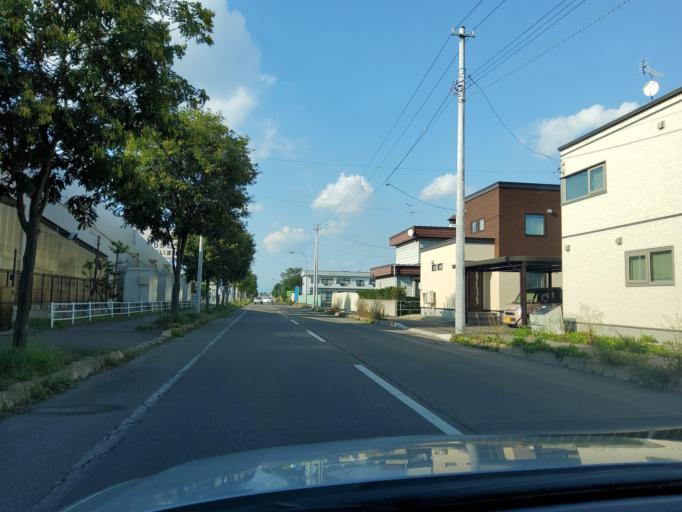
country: JP
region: Hokkaido
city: Obihiro
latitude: 42.8870
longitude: 143.2008
